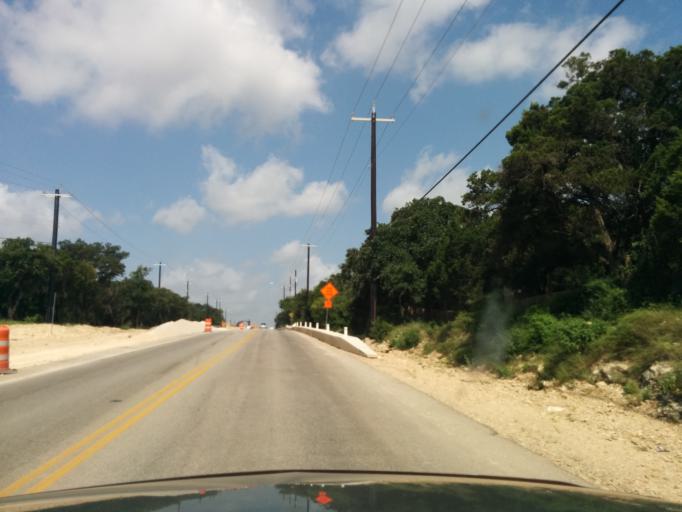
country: US
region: Texas
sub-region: Bexar County
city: Helotes
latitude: 29.5723
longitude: -98.6217
